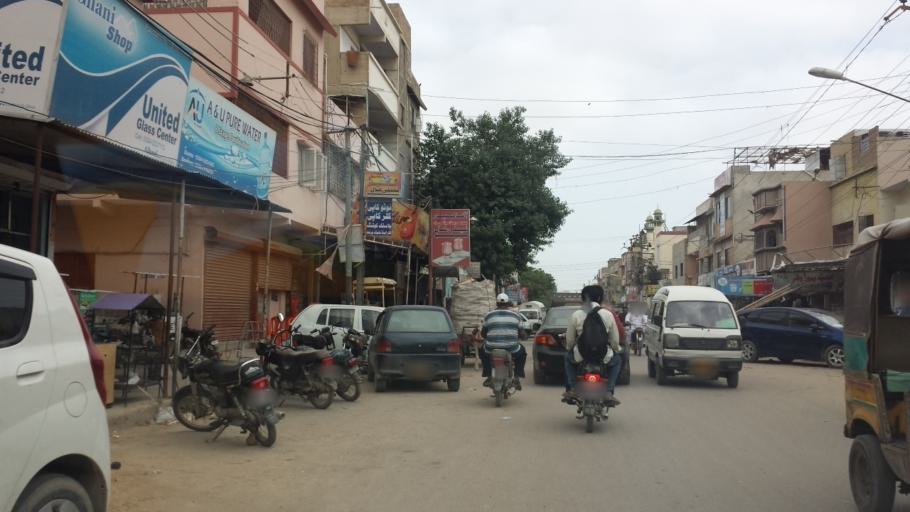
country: PK
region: Sindh
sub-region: Karachi District
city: Karachi
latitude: 24.9433
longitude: 67.0782
